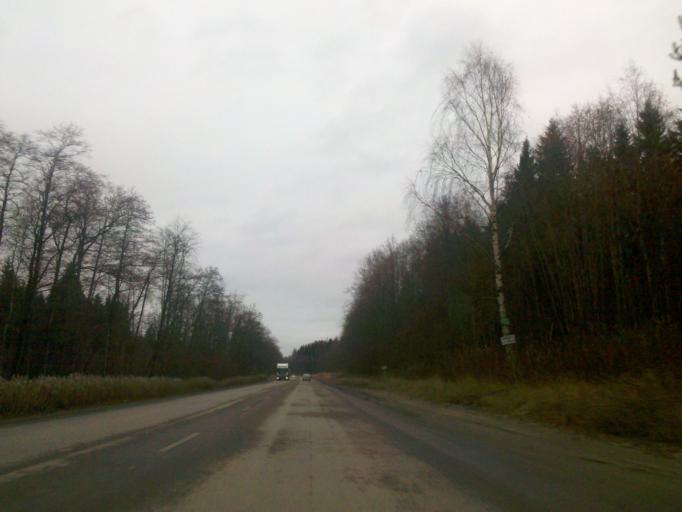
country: RU
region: Republic of Karelia
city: Petrozavodsk
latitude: 61.8208
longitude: 34.2463
